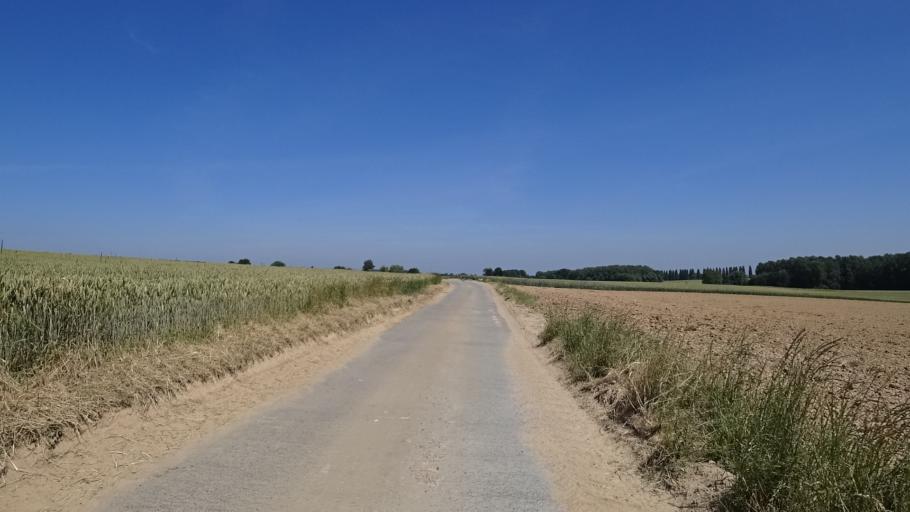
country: BE
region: Wallonia
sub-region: Province du Brabant Wallon
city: Perwez
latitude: 50.6496
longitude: 4.8391
